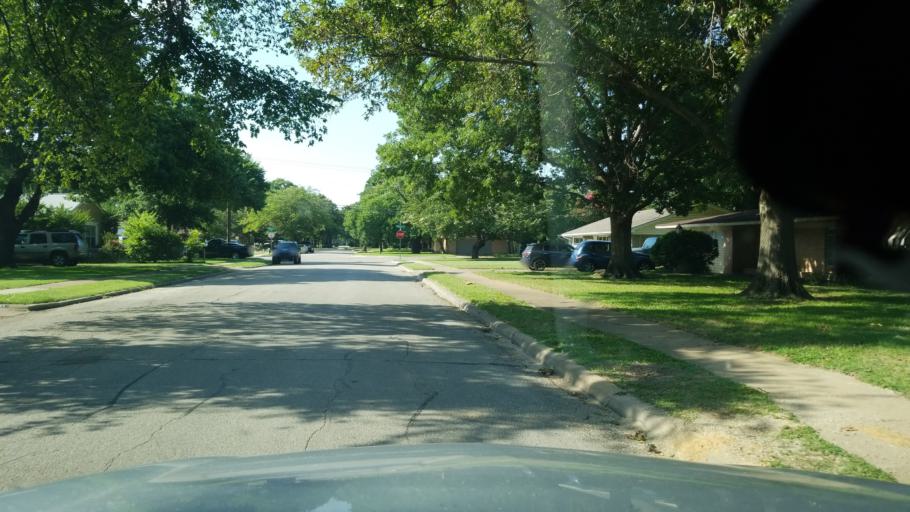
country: US
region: Texas
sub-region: Dallas County
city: Irving
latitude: 32.8217
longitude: -96.9705
